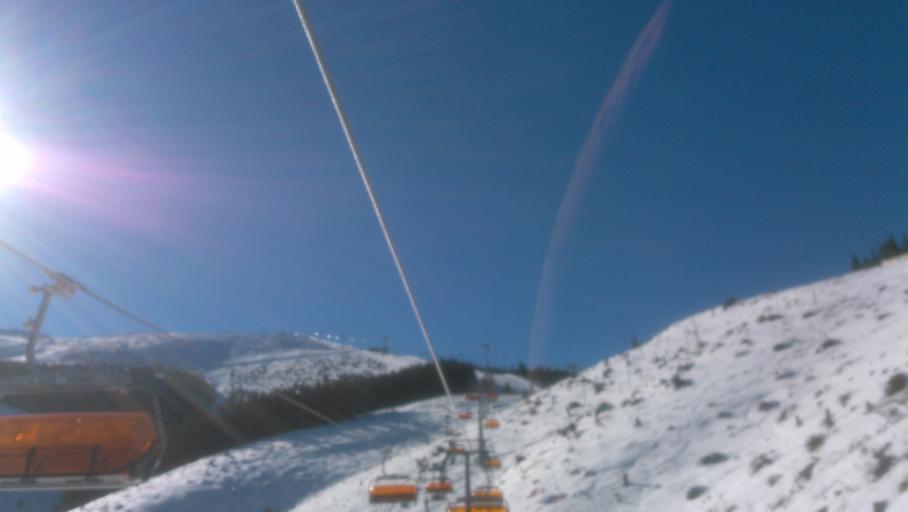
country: SK
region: Zilinsky
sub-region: Okres Liptovsky Mikulas
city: Liptovsky Mikulas
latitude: 48.9658
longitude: 19.5933
